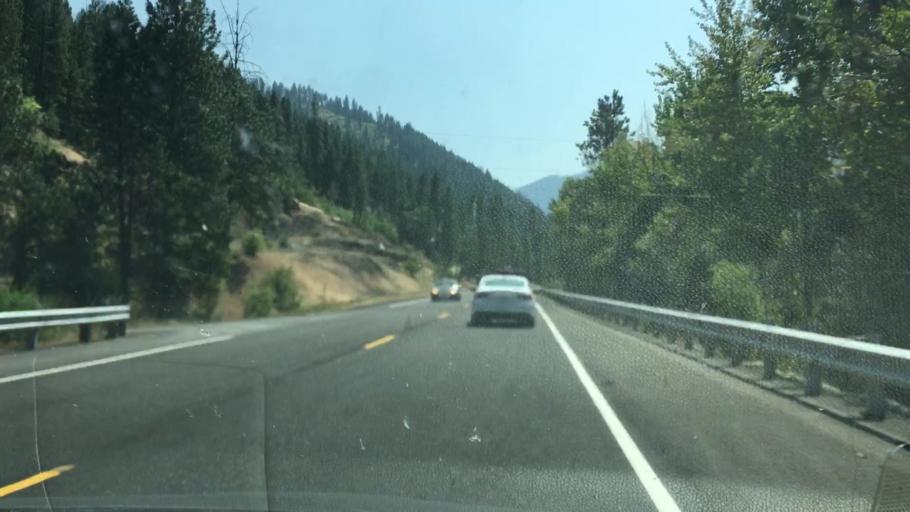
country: US
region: Idaho
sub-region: Valley County
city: McCall
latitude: 45.1802
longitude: -116.3015
